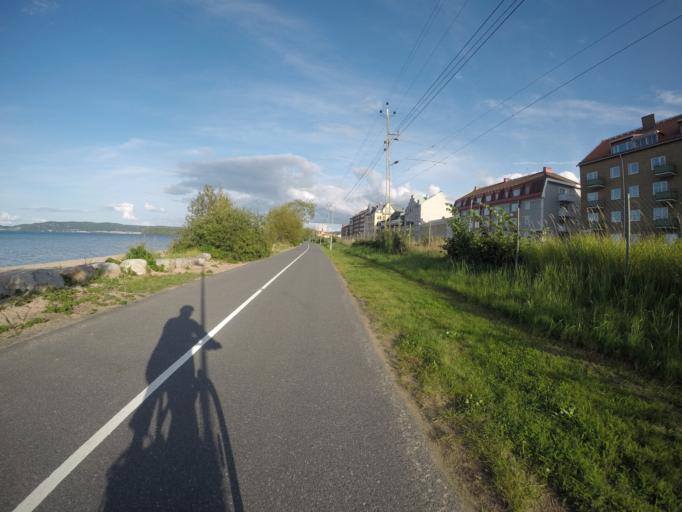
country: SE
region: Joenkoeping
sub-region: Jonkopings Kommun
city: Jonkoping
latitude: 57.7825
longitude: 14.1821
